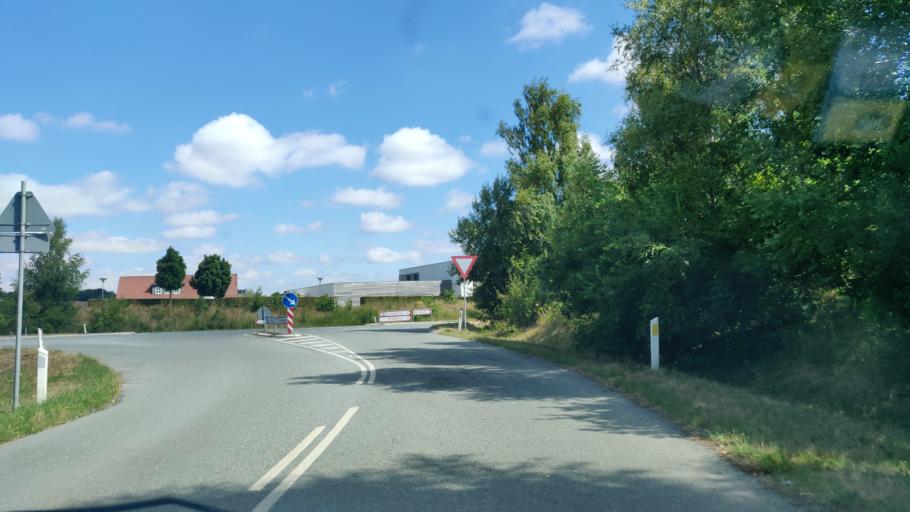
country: DK
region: South Denmark
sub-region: Kolding Kommune
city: Kolding
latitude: 55.5116
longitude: 9.5101
